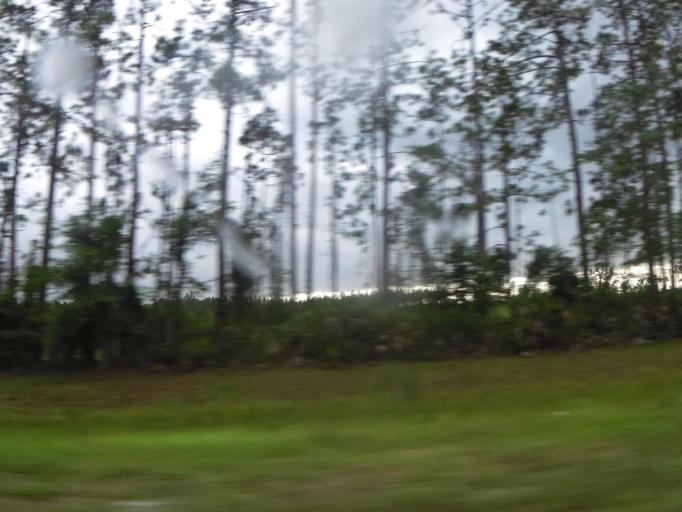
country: US
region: Florida
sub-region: Baker County
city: Macclenny
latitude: 30.2371
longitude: -82.3036
